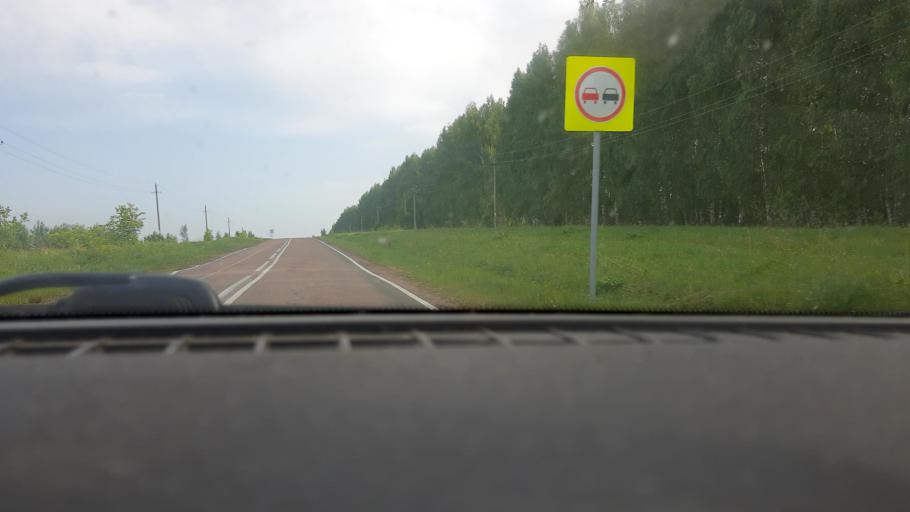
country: RU
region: Bashkortostan
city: Ulukulevo
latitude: 54.5670
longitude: 56.4313
